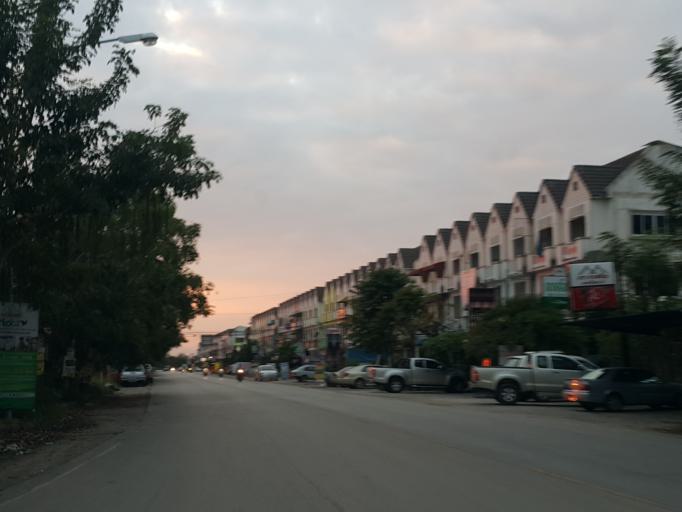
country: TH
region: Lampang
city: Lampang
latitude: 18.2633
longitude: 99.4957
